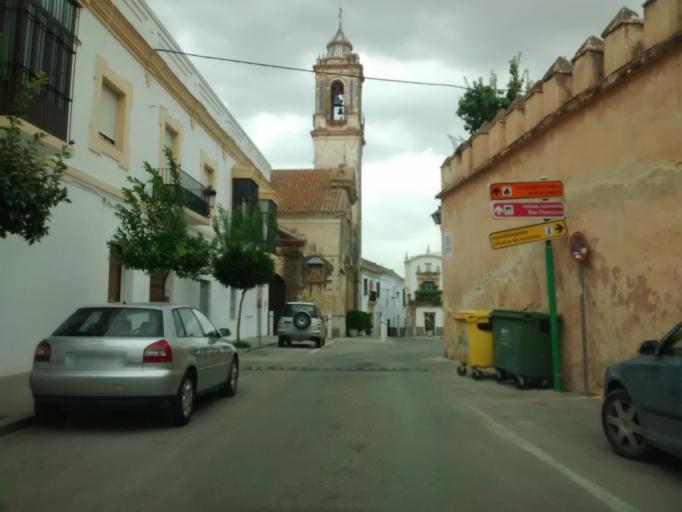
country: ES
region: Andalusia
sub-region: Provincia de Cadiz
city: Bornos
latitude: 36.8154
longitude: -5.7432
